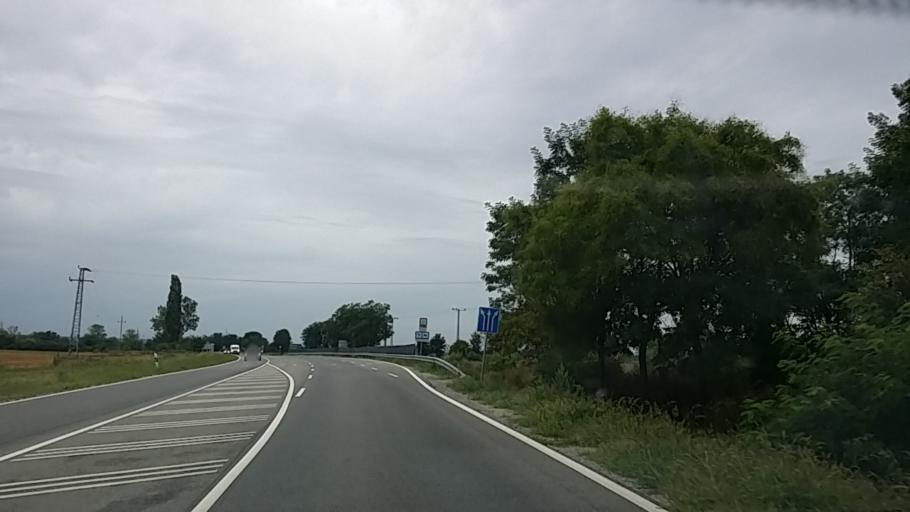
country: HU
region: Gyor-Moson-Sopron
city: Fertoszentmiklos
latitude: 47.5973
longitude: 16.8230
